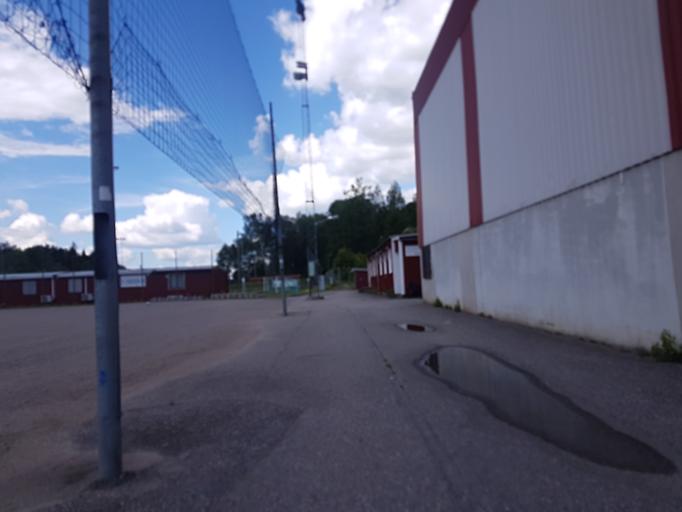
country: SE
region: Soedermanland
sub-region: Gnesta Kommun
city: Gnesta
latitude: 59.0353
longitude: 17.3210
